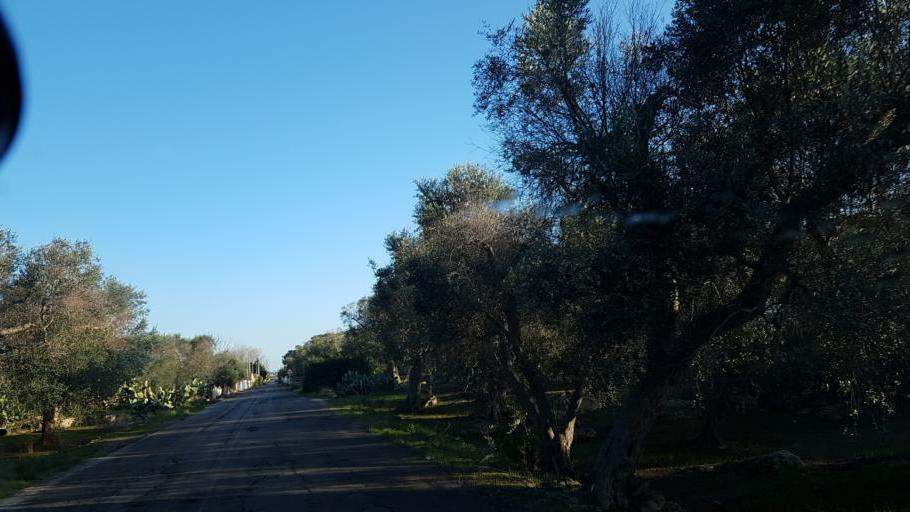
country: IT
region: Apulia
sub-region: Provincia di Brindisi
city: Torchiarolo
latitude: 40.5035
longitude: 18.1077
